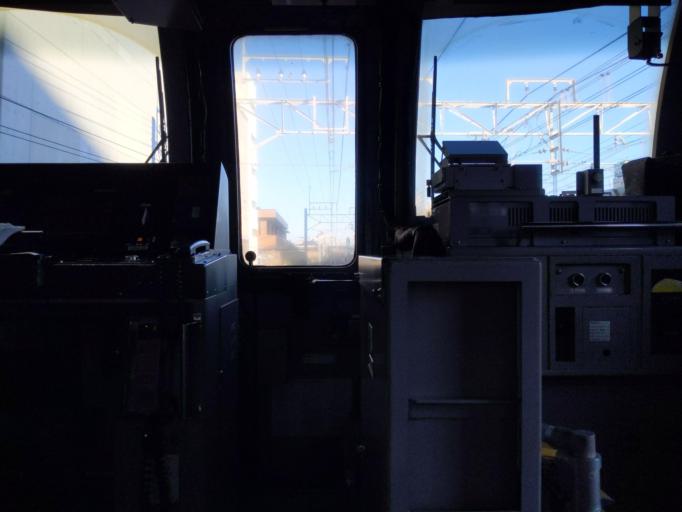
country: JP
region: Chiba
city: Funabashi
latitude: 35.7061
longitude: 139.9626
